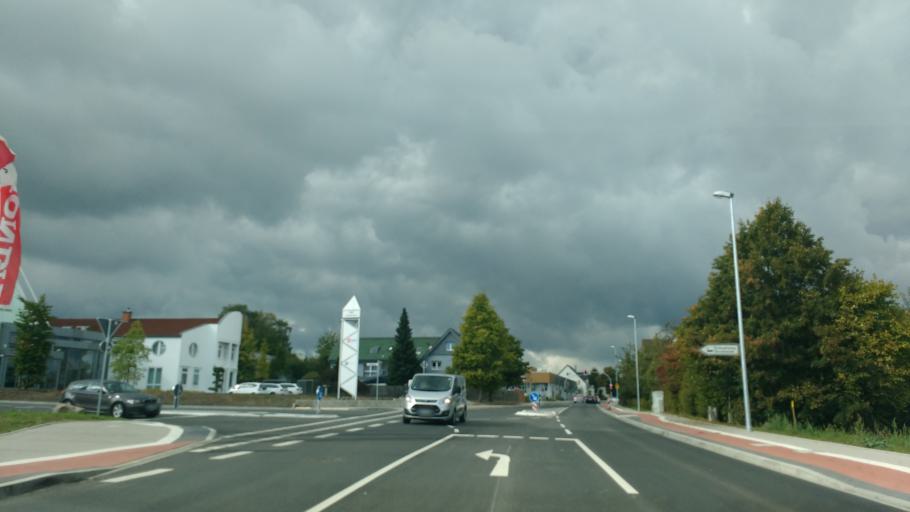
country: DE
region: North Rhine-Westphalia
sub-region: Regierungsbezirk Detmold
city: Herford
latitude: 52.1230
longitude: 8.6388
